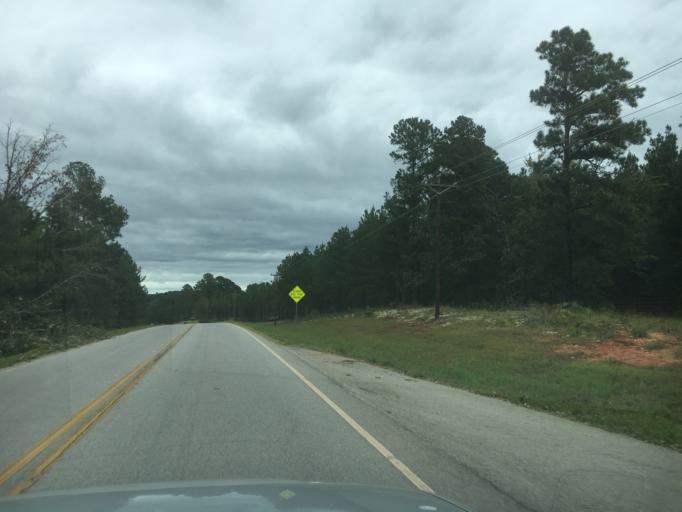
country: US
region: Georgia
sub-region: Lincoln County
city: Lincolnton
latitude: 33.7242
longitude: -82.5825
